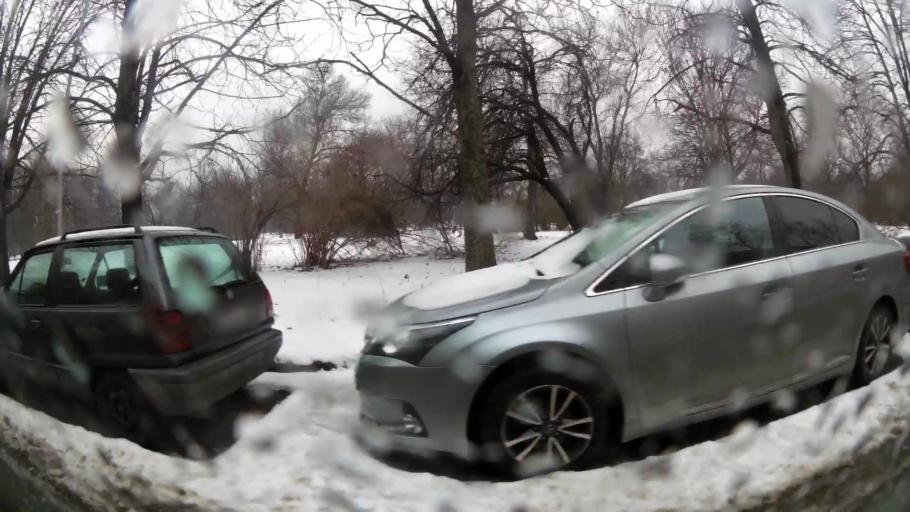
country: BG
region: Sofia-Capital
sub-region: Stolichna Obshtina
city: Sofia
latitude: 42.6749
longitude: 23.2757
